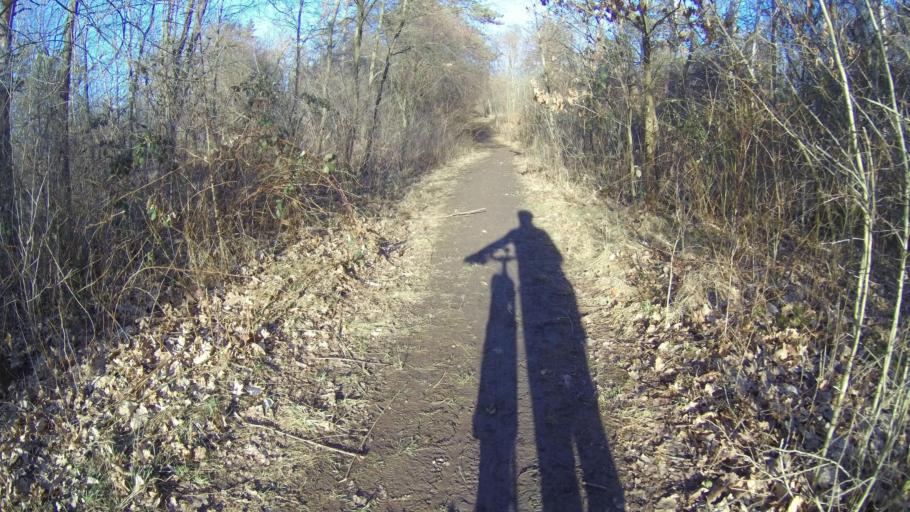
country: CZ
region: Central Bohemia
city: Neratovice
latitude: 50.2305
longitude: 14.5039
